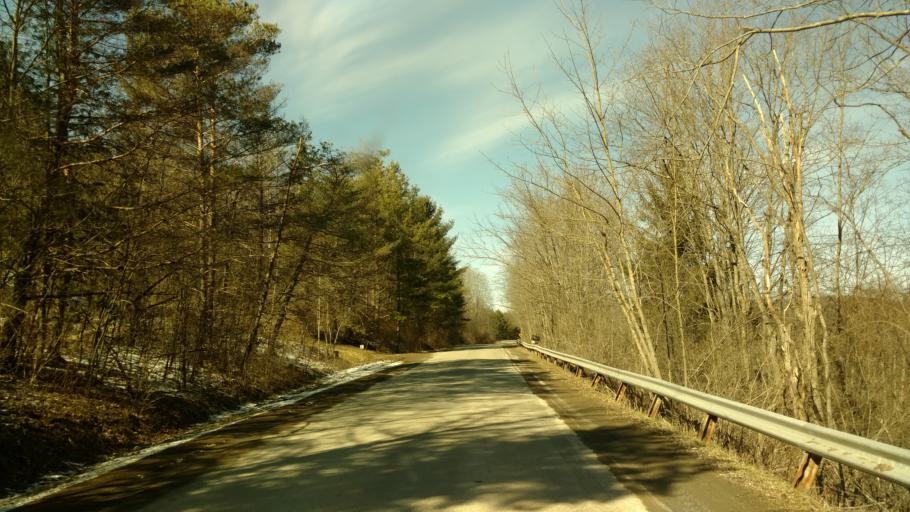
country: US
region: New York
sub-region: Allegany County
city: Wellsville
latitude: 42.0964
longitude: -77.9386
